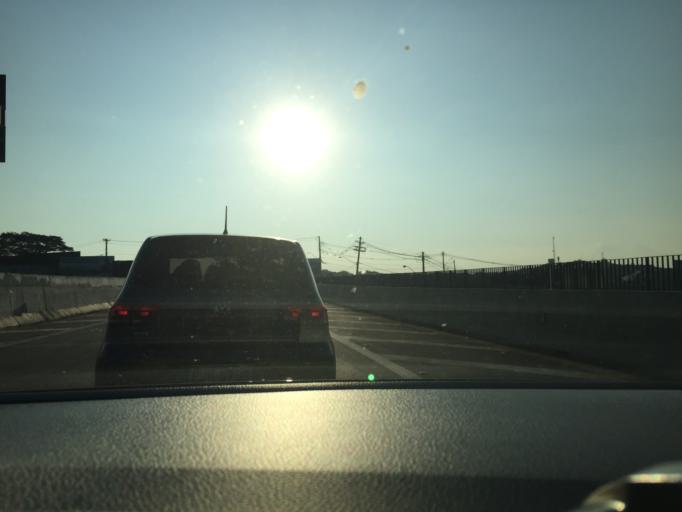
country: BR
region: Sao Paulo
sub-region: Louveira
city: Louveira
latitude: -23.0954
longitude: -46.9669
